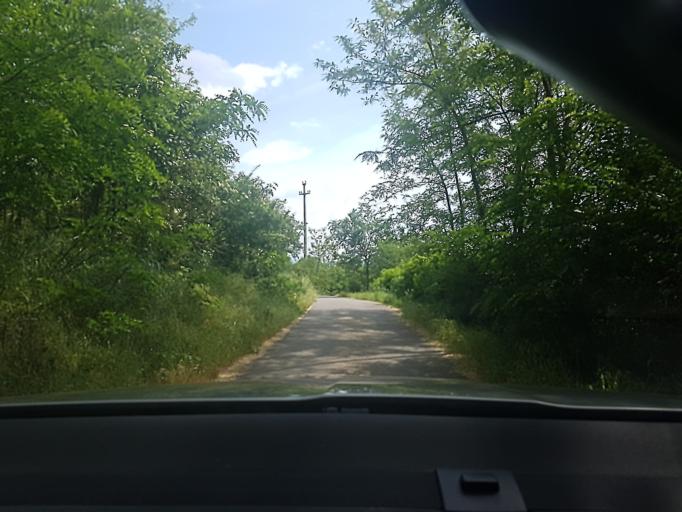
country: RO
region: Hunedoara
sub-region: Comuna Calan
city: Calan
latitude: 45.7220
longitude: 23.0182
